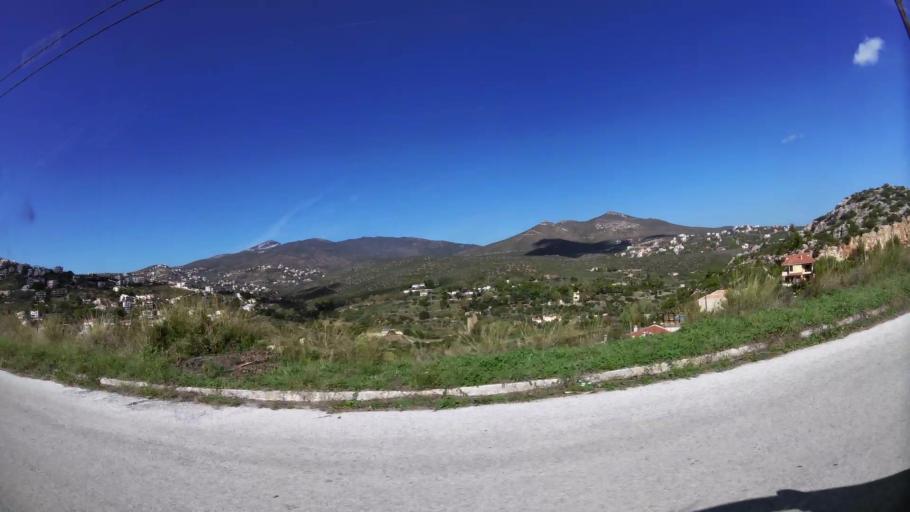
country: GR
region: Attica
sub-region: Nomarchia Anatolikis Attikis
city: Dhrafi
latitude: 38.0187
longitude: 23.9144
